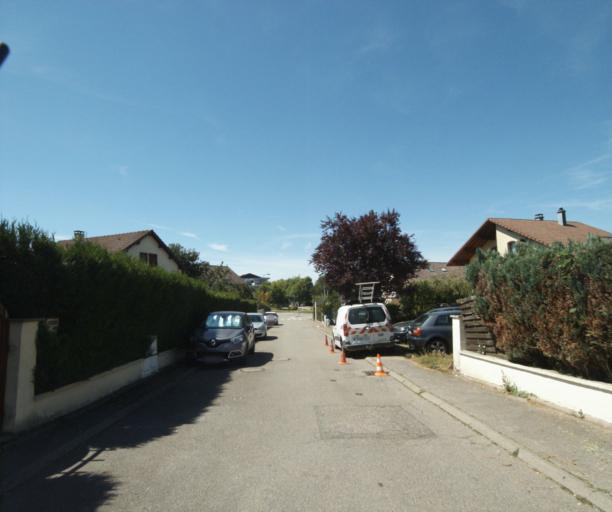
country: FR
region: Lorraine
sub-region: Departement des Vosges
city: Epinal
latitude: 48.1922
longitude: 6.4629
